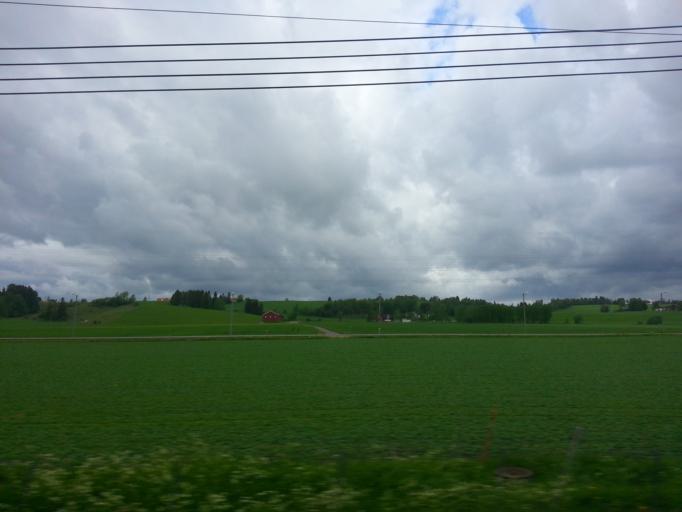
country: NO
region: Akershus
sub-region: Skedsmo
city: Leirsund
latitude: 59.9791
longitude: 11.0719
